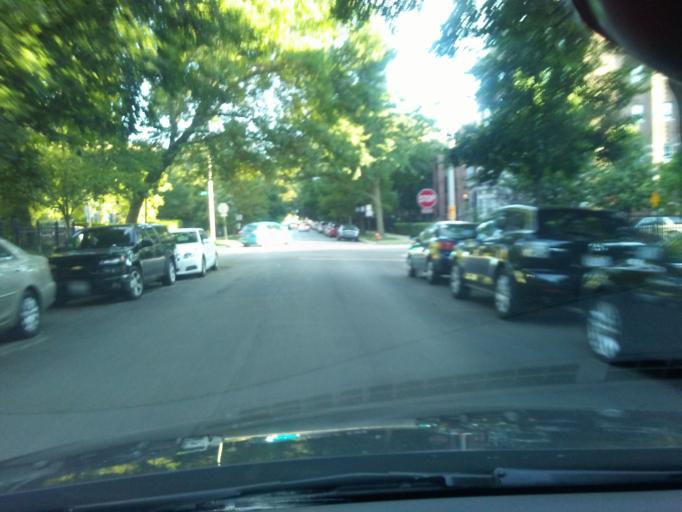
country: US
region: Illinois
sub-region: Cook County
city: Lincolnwood
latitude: 41.9668
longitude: -87.6640
